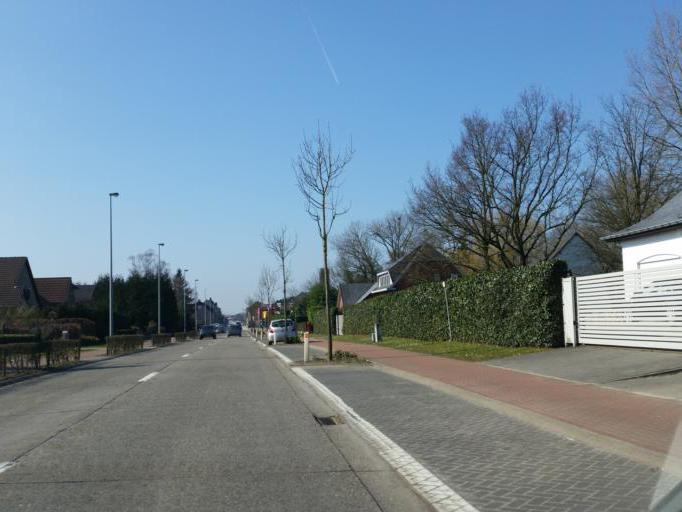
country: BE
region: Flanders
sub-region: Provincie Oost-Vlaanderen
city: Temse
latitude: 51.1287
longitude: 4.2365
